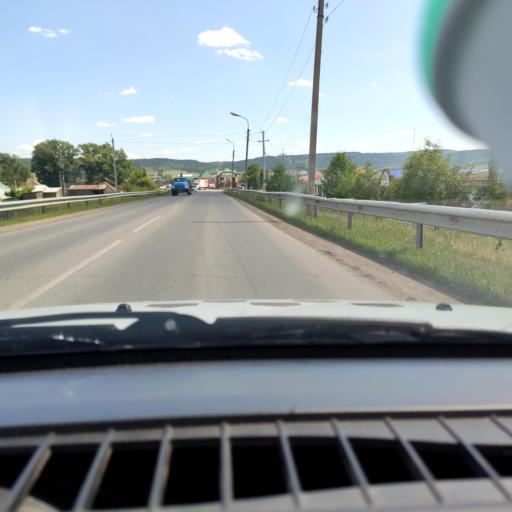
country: RU
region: Bashkortostan
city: Mesyagutovo
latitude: 55.5305
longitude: 58.2551
